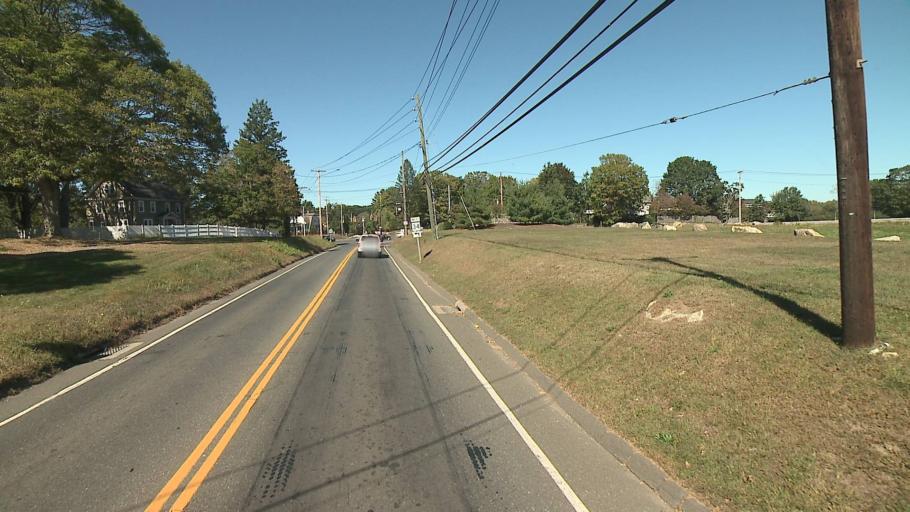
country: US
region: Connecticut
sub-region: New Haven County
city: Orange
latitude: 41.3100
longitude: -73.0465
